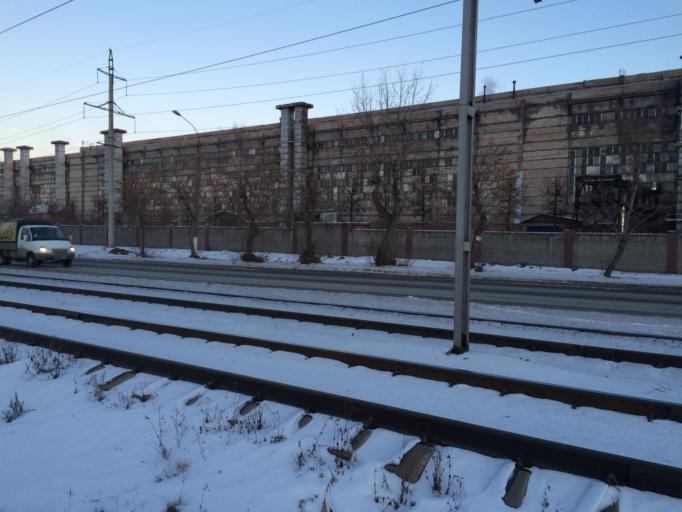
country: RU
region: Chelyabinsk
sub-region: Gorod Magnitogorsk
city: Magnitogorsk
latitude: 53.3999
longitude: 59.0244
